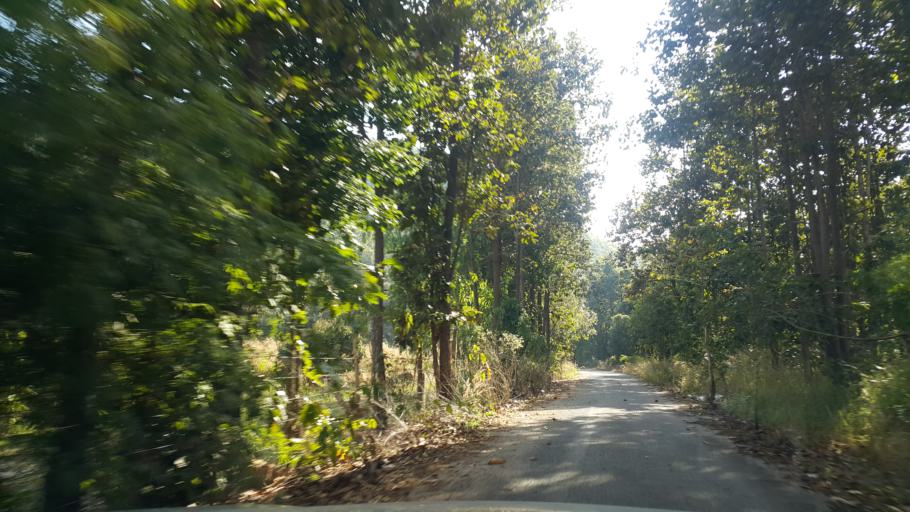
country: TH
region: Lamphun
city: Ban Thi
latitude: 18.5837
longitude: 99.1323
